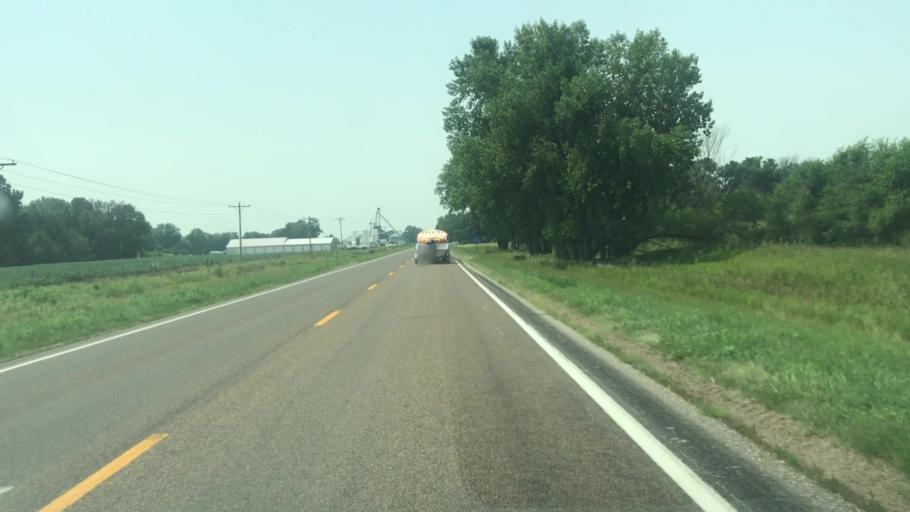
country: US
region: Nebraska
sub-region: Buffalo County
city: Ravenna
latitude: 41.0758
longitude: -98.7075
